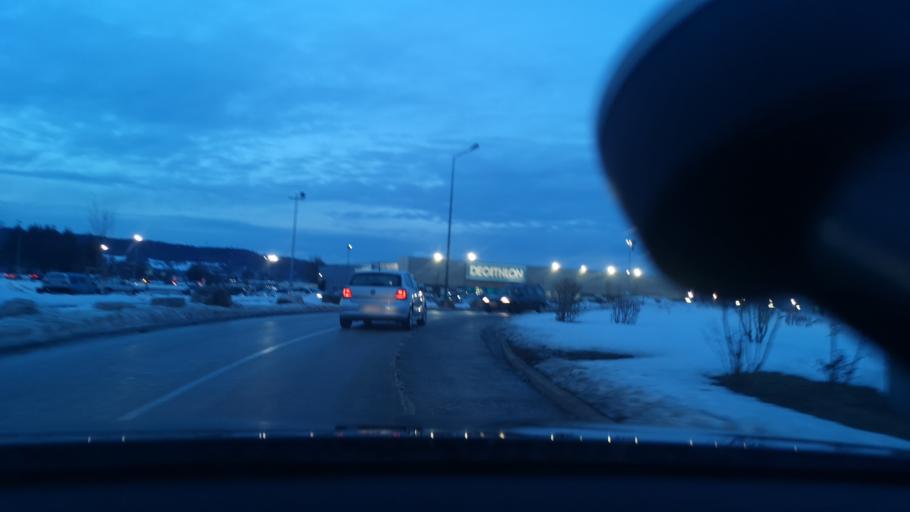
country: FR
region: Franche-Comte
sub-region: Departement du Doubs
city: Doubs
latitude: 46.9231
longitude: 6.3399
